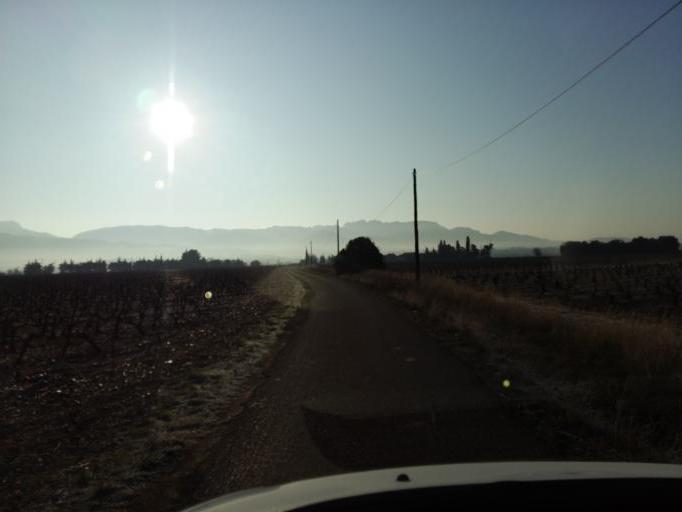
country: FR
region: Provence-Alpes-Cote d'Azur
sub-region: Departement du Vaucluse
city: Sablet
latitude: 44.2046
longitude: 4.9794
